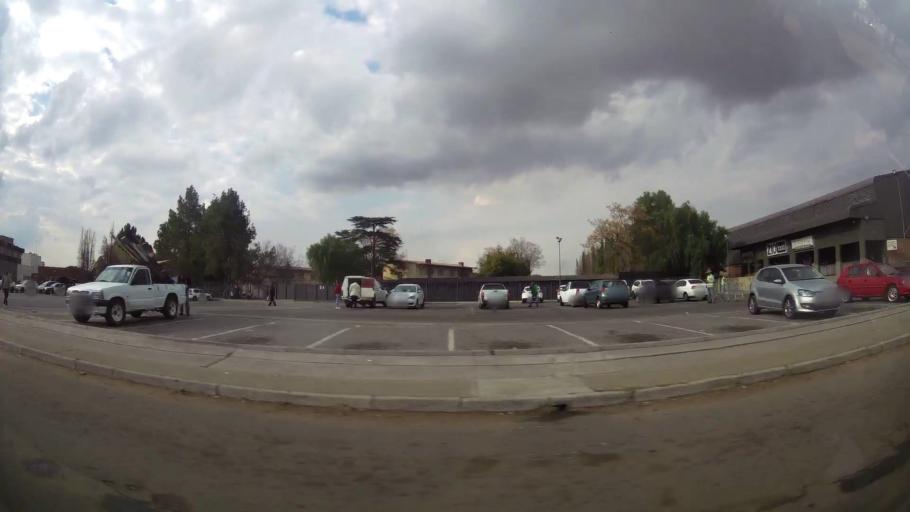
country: ZA
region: Orange Free State
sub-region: Fezile Dabi District Municipality
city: Sasolburg
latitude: -26.8203
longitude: 27.8344
